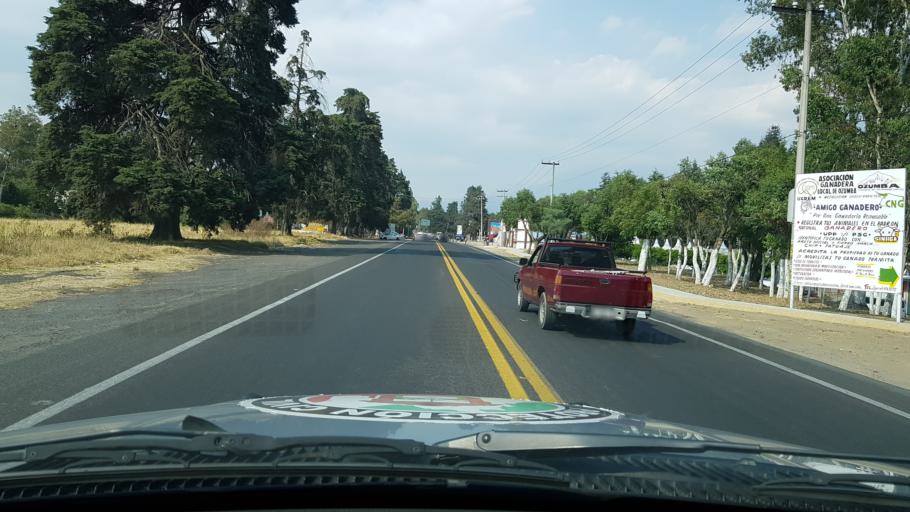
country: MX
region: Mexico
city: Ozumba de Alzate
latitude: 19.0517
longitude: -98.7903
